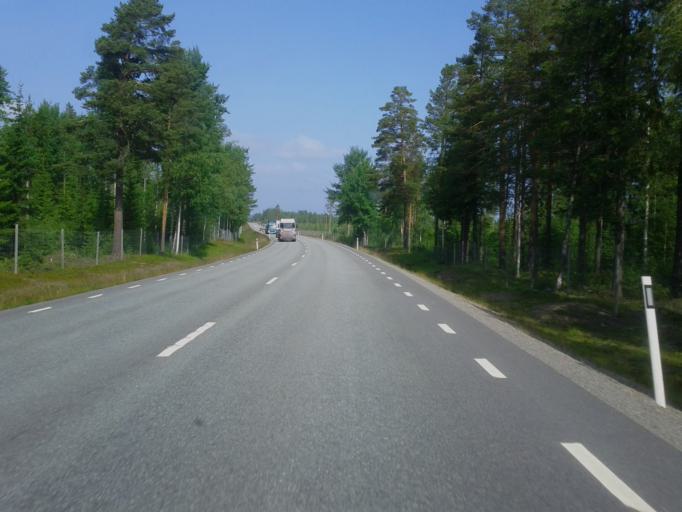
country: SE
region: Vaesterbotten
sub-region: Skelleftea Kommun
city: Burea
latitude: 64.5851
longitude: 21.2189
